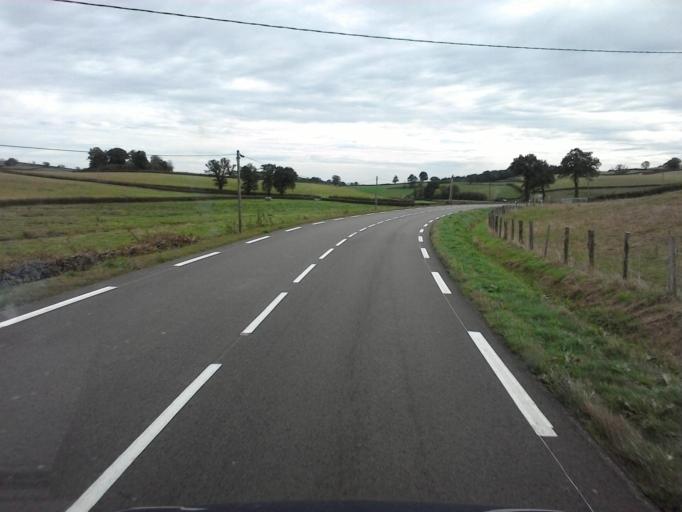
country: FR
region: Bourgogne
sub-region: Departement de Saone-et-Loire
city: Saint-Eusebe
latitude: 46.5991
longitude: 4.4836
